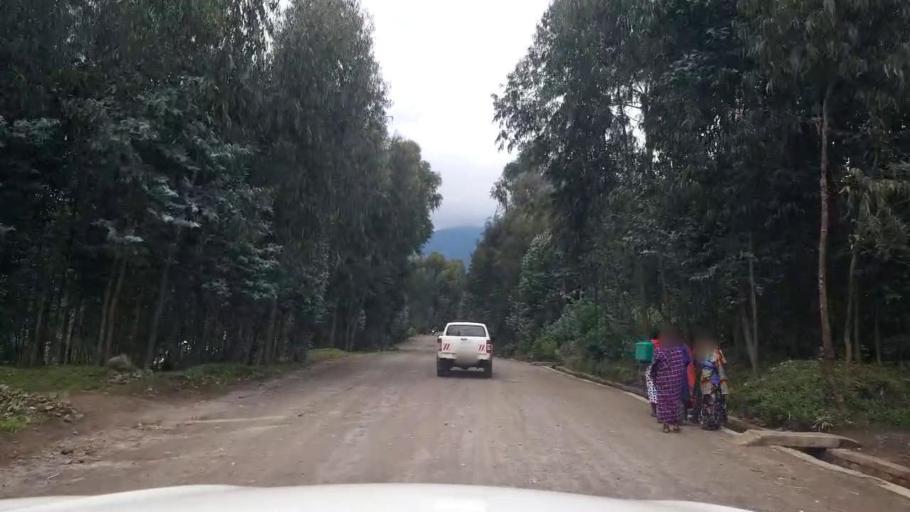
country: RW
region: Northern Province
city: Musanze
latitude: -1.4432
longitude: 29.5363
